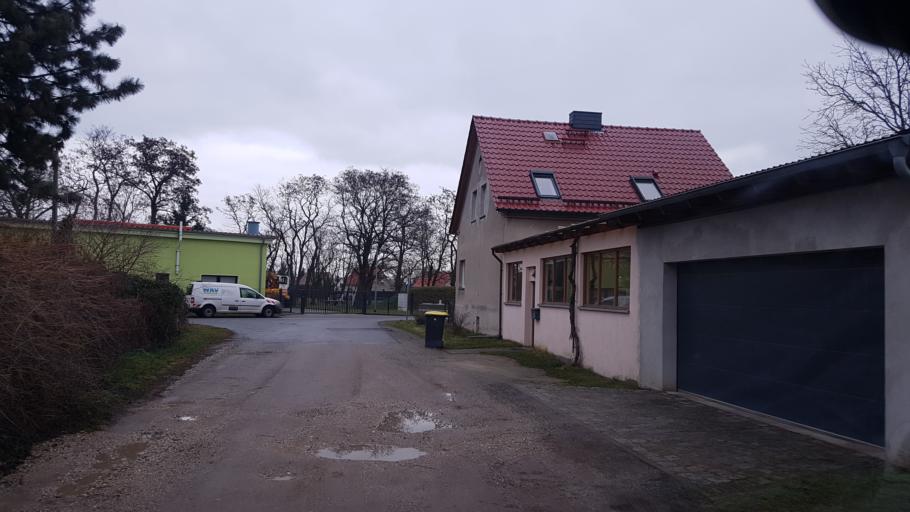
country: DE
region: Brandenburg
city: Doberlug-Kirchhain
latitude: 51.6068
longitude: 13.5584
